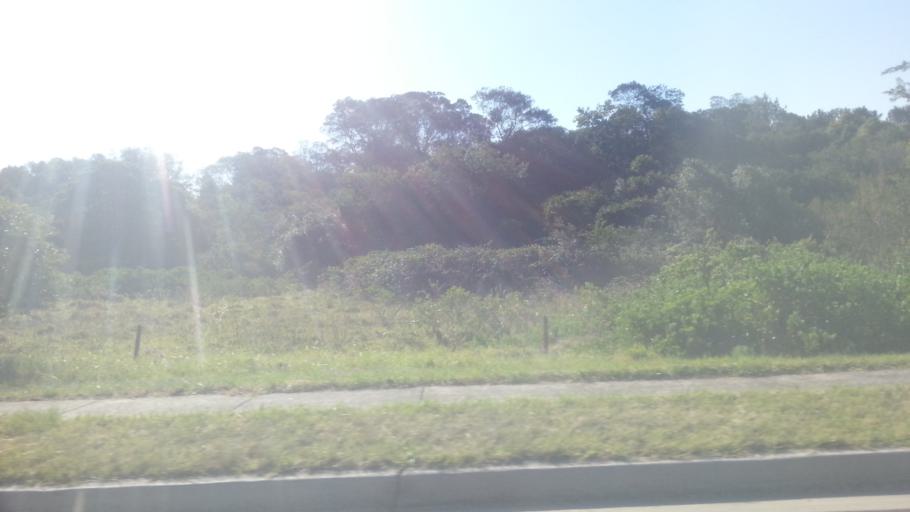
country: AU
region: New South Wales
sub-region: Wollongong
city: Berkeley
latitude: -34.4668
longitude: 150.8531
